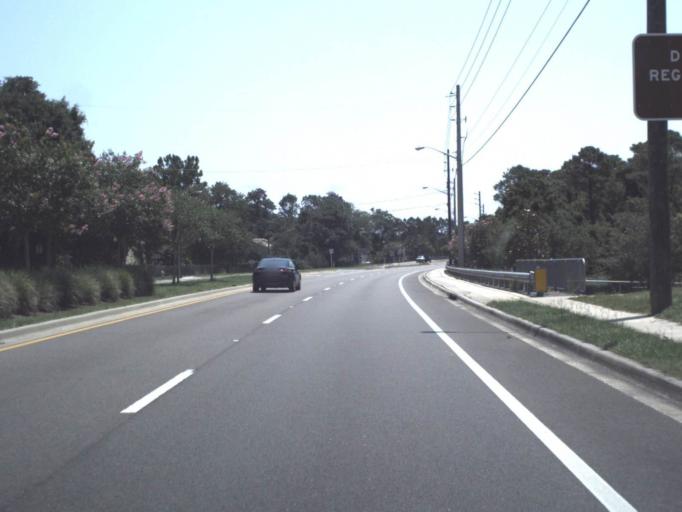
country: US
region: Florida
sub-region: Duval County
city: Atlantic Beach
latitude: 30.3597
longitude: -81.5086
